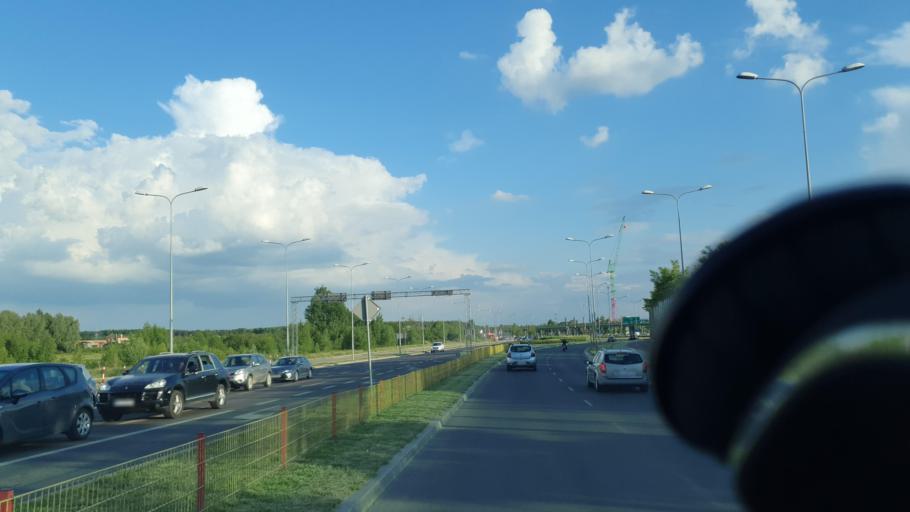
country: PL
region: Podlasie
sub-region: Bialystok
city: Bialystok
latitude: 53.1438
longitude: 23.2018
